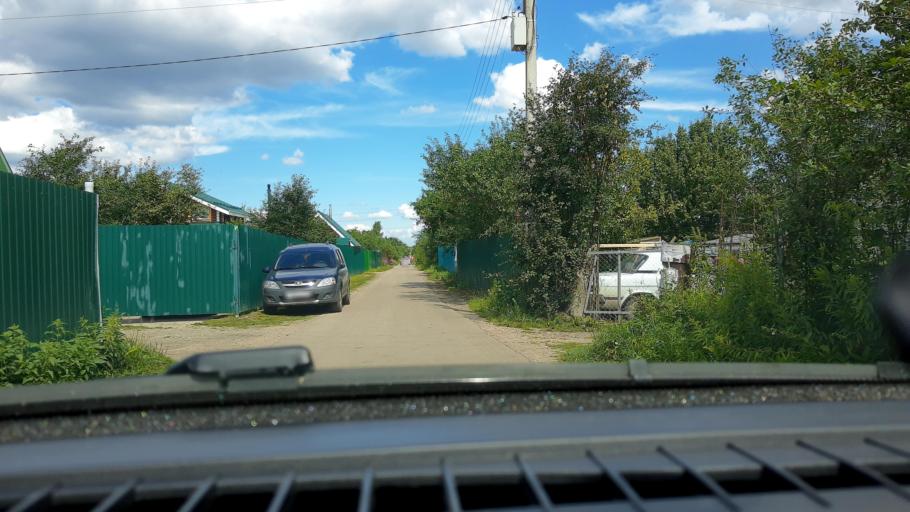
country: RU
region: Nizjnij Novgorod
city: Gorbatovka
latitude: 56.2544
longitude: 43.8139
